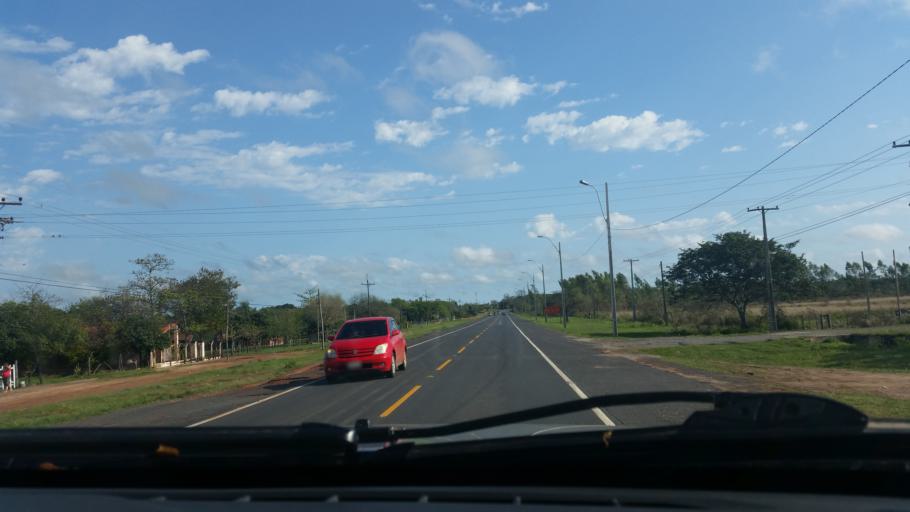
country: PY
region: Presidente Hayes
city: Benjamin Aceval
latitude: -25.0321
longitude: -57.5522
